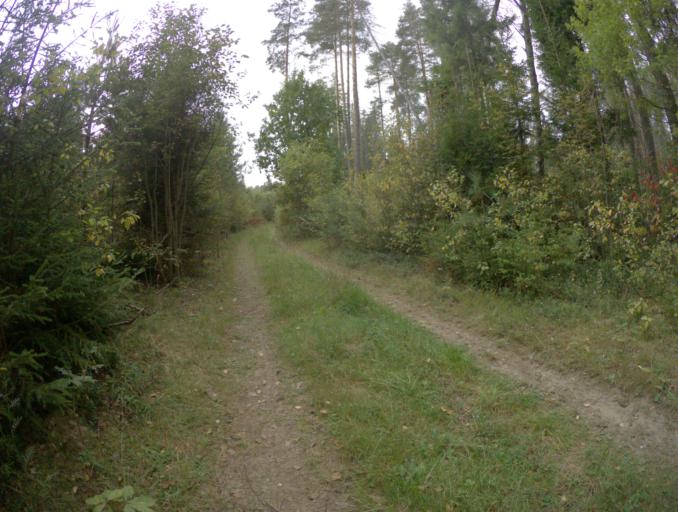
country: RU
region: Vladimir
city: Golovino
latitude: 55.9911
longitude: 40.4681
